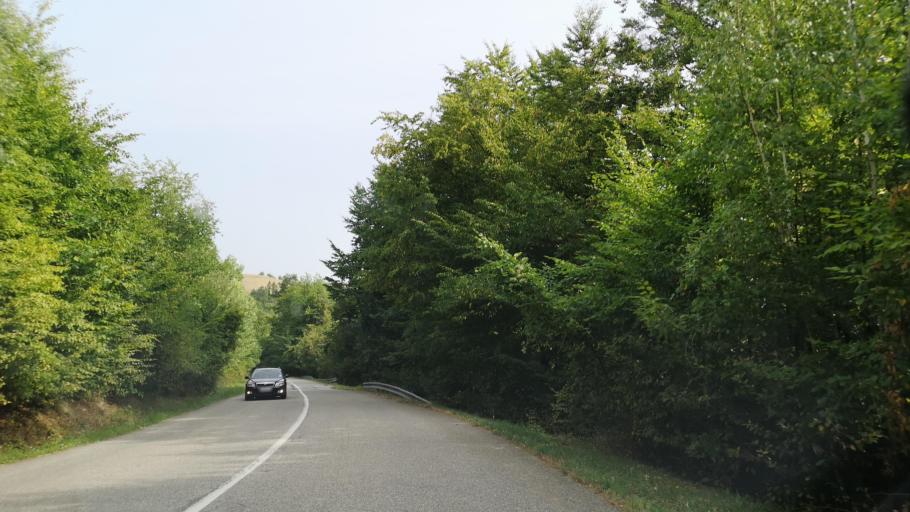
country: SK
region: Banskobystricky
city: Revuca
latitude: 48.5733
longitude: 20.0348
